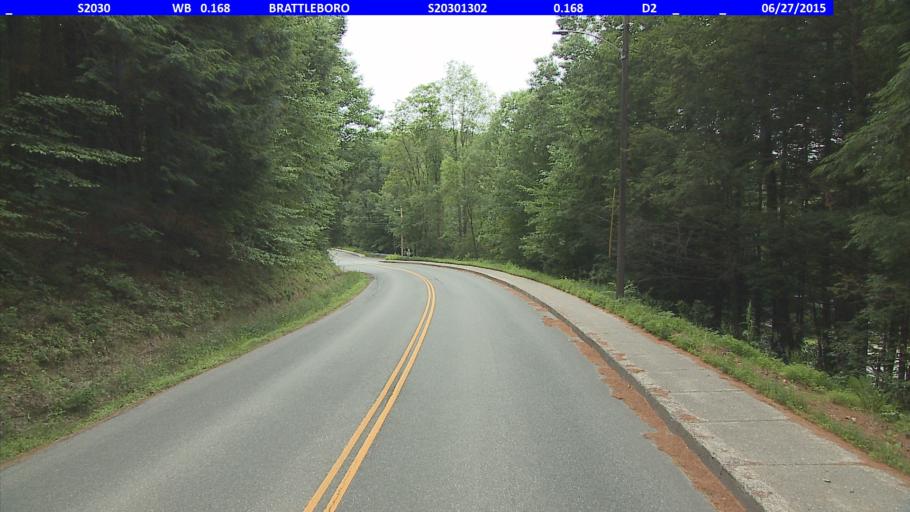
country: US
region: Vermont
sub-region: Windham County
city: Brattleboro
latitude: 42.8457
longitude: -72.5801
